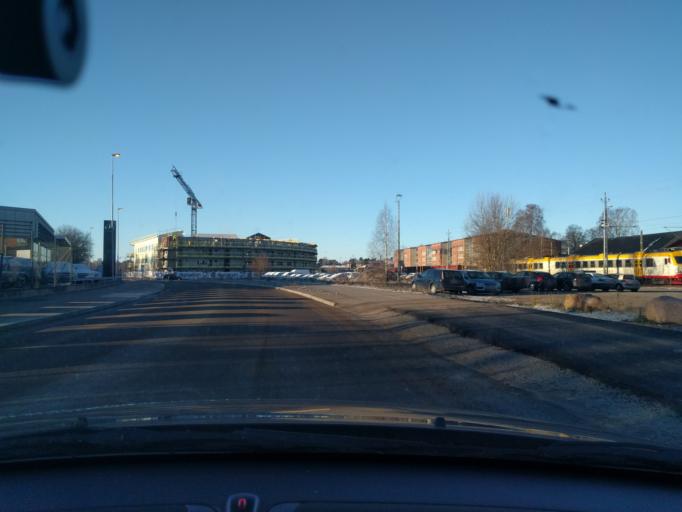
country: SE
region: Kronoberg
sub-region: Vaxjo Kommun
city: Vaexjoe
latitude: 56.8759
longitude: 14.7934
